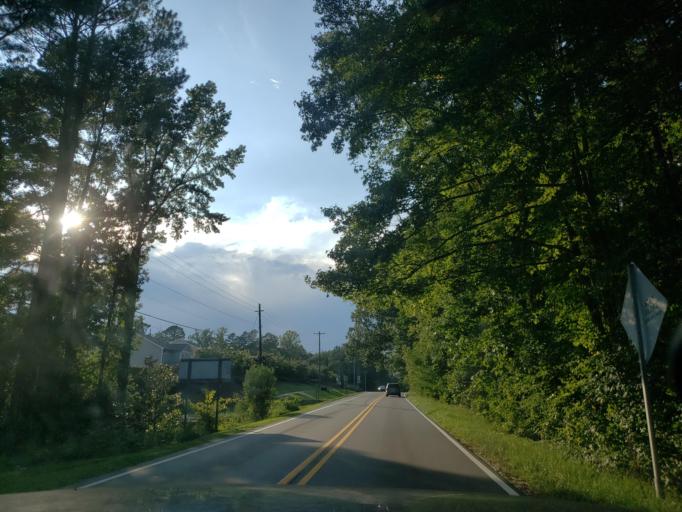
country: US
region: North Carolina
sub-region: Durham County
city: Durham
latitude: 35.9847
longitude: -78.9596
